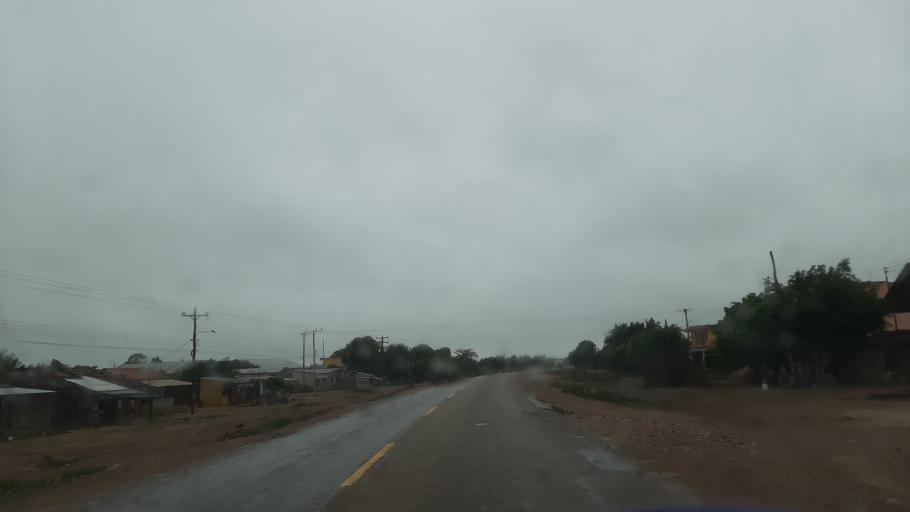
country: BO
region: Santa Cruz
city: Okinawa Numero Uno
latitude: -16.8068
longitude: -62.5999
